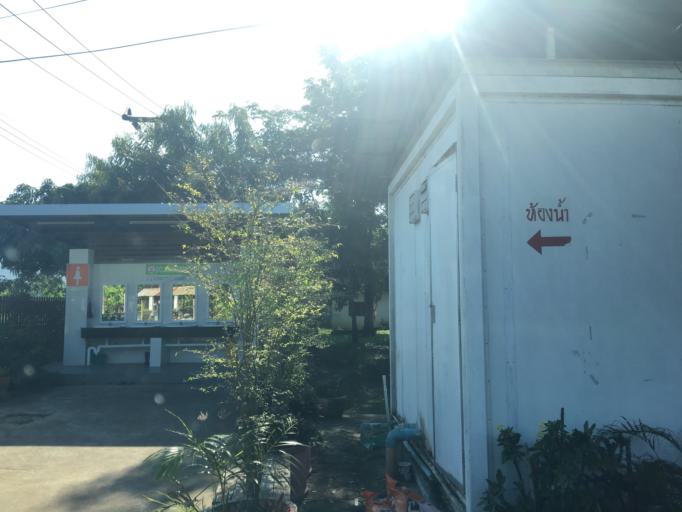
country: TH
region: Phayao
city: Chun
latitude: 19.3305
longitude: 100.1402
